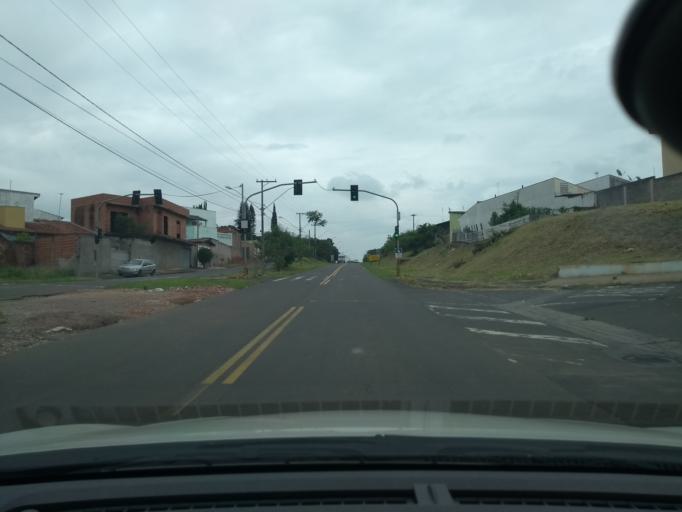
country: BR
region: Sao Paulo
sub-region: Rio Claro
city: Rio Claro
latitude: -22.3737
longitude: -47.5389
